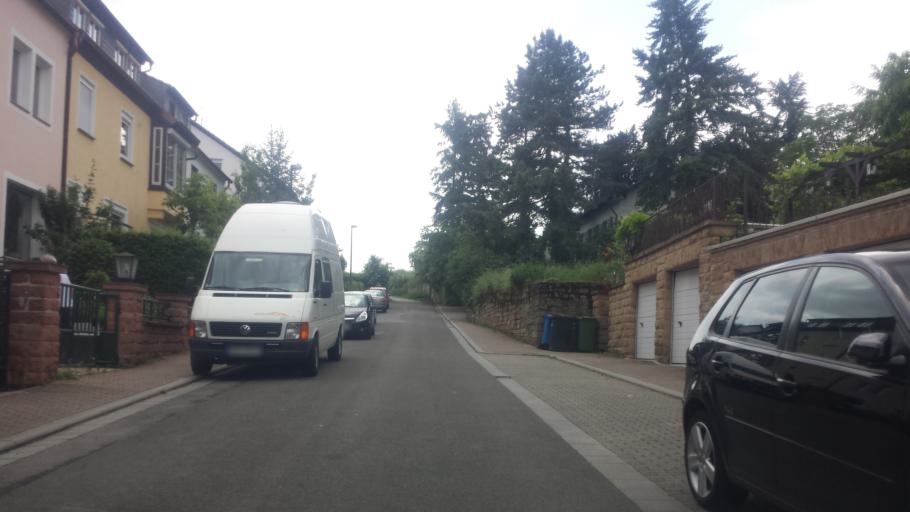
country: DE
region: Rheinland-Pfalz
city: Bad Duerkheim
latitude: 49.4545
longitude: 8.1723
